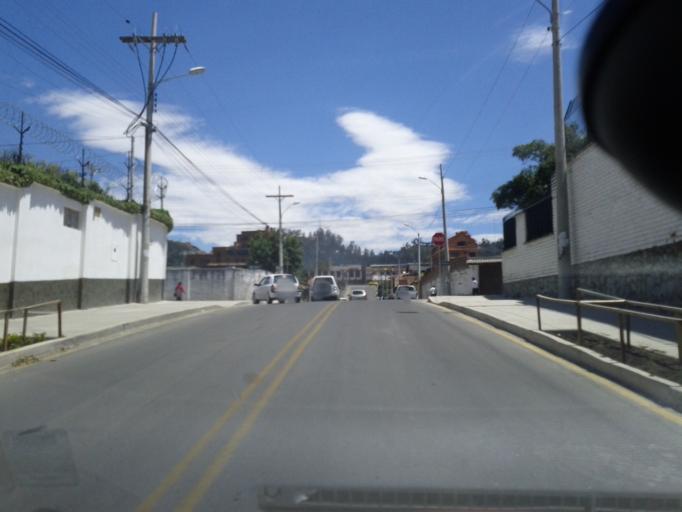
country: EC
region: Azuay
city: Cuenca
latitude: -2.9079
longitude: -79.0096
